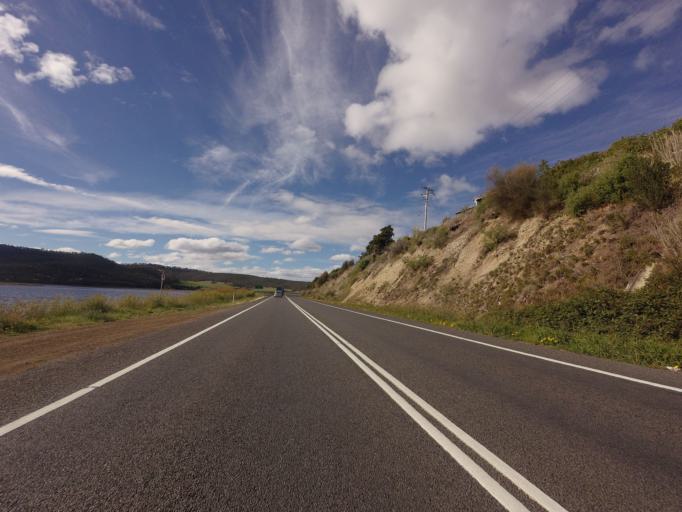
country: AU
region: Tasmania
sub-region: Brighton
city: Bridgewater
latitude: -42.7426
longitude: 147.1934
